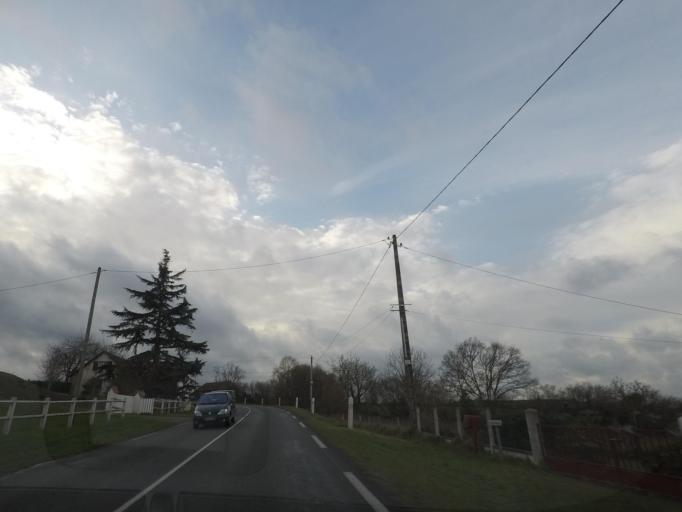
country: FR
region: Pays de la Loire
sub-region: Departement de la Sarthe
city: Vibraye
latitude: 48.1133
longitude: 0.7076
